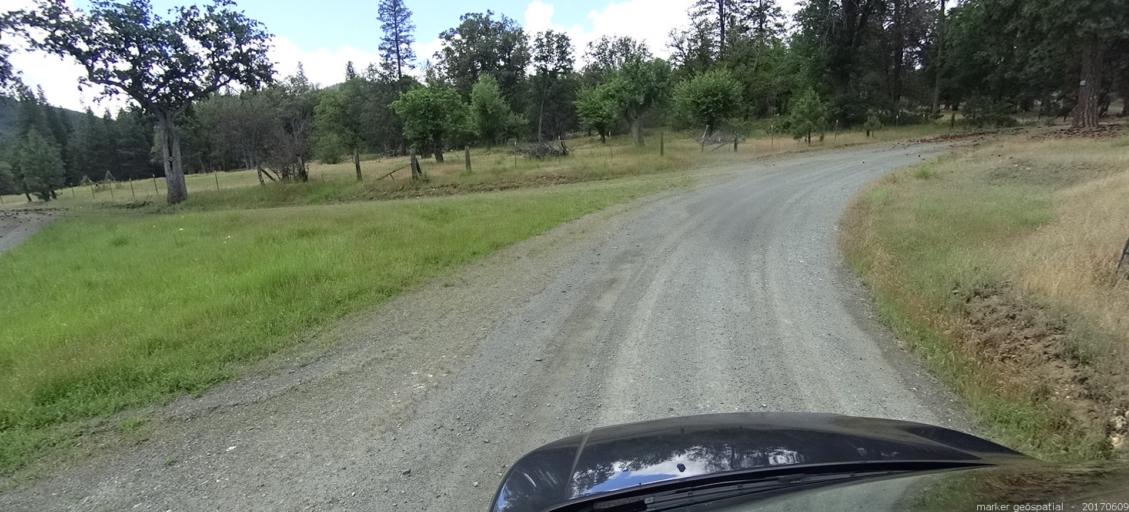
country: US
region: California
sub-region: Siskiyou County
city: Yreka
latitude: 41.3686
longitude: -122.8736
